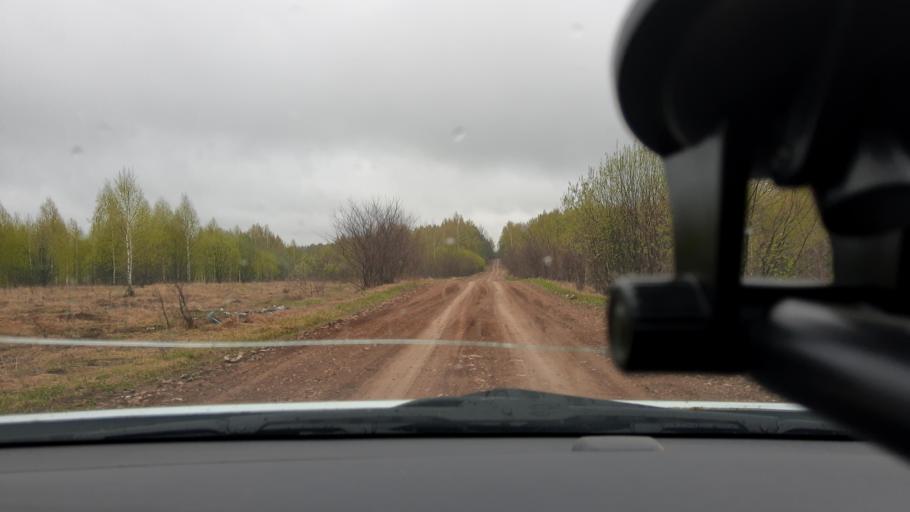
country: RU
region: Bashkortostan
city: Pavlovka
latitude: 55.4364
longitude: 56.3605
